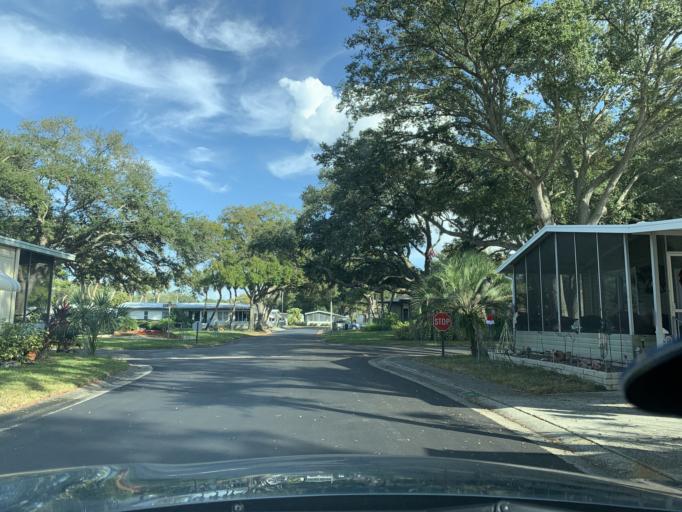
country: US
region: Florida
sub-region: Pinellas County
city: Largo
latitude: 27.8970
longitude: -82.7815
